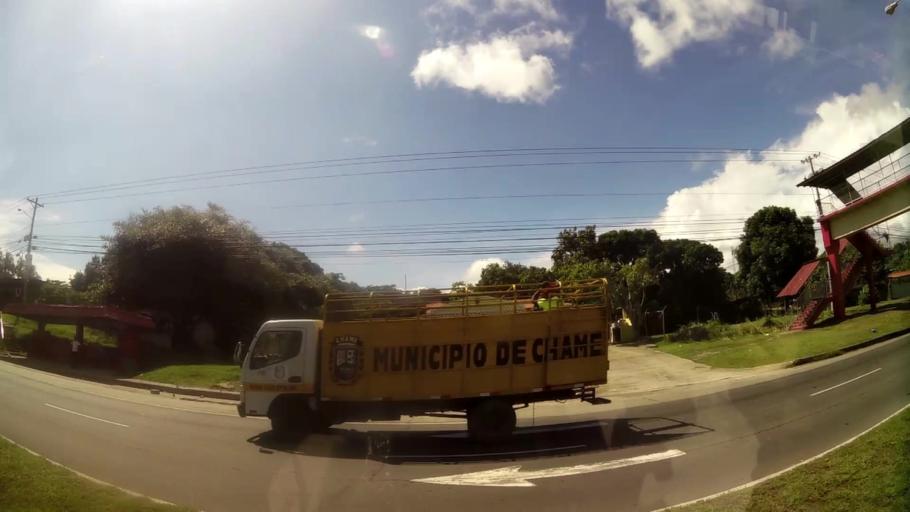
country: PA
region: Panama
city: Chame
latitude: 8.5794
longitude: -79.8843
